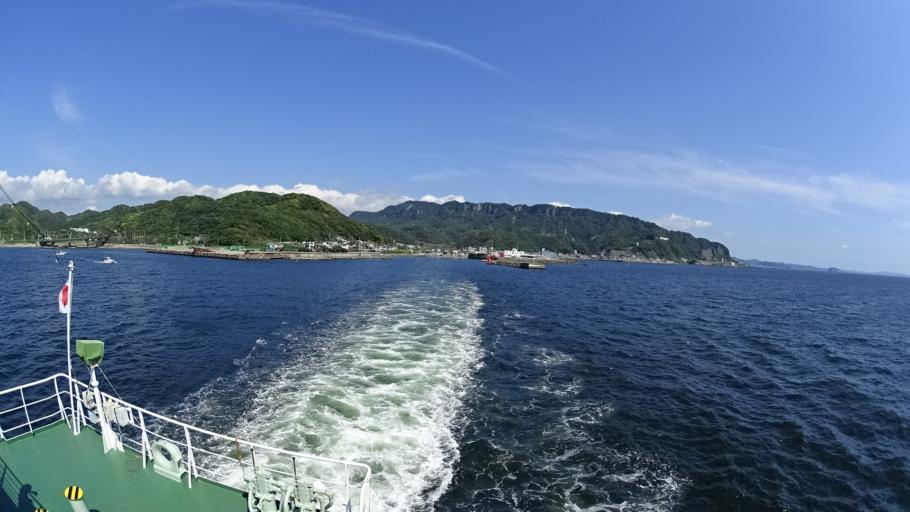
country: JP
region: Chiba
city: Futtsu
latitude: 35.1726
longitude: 139.8130
